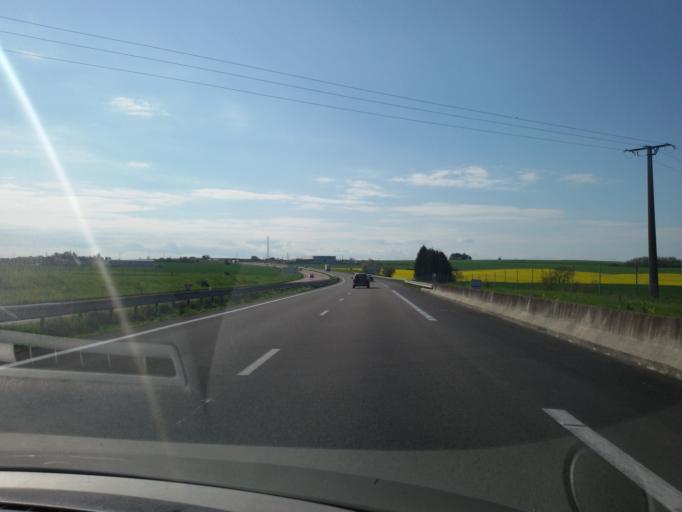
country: FR
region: Bourgogne
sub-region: Departement de l'Yonne
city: Joux-la-Ville
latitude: 47.6687
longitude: 3.8682
